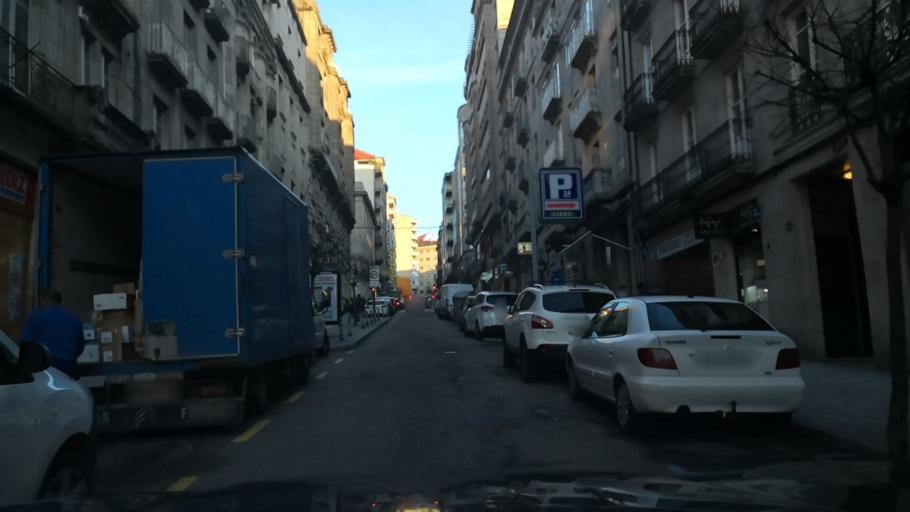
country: ES
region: Galicia
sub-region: Provincia de Ourense
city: Ourense
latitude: 42.3396
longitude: -7.8659
